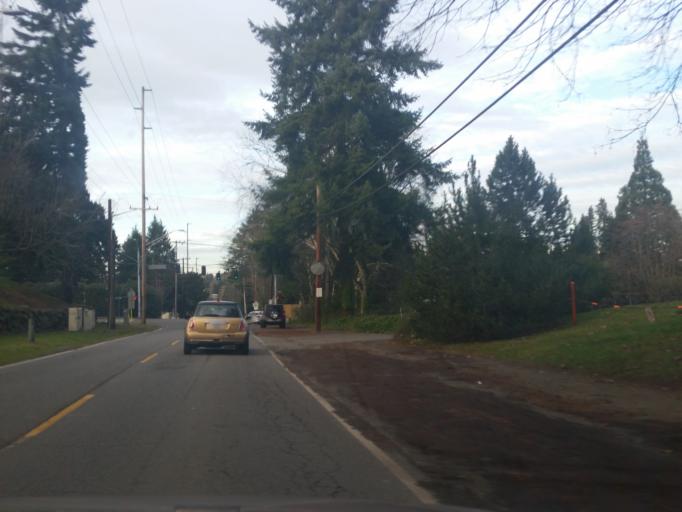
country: US
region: Washington
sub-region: King County
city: Shoreline
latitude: 47.7333
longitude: -122.3289
